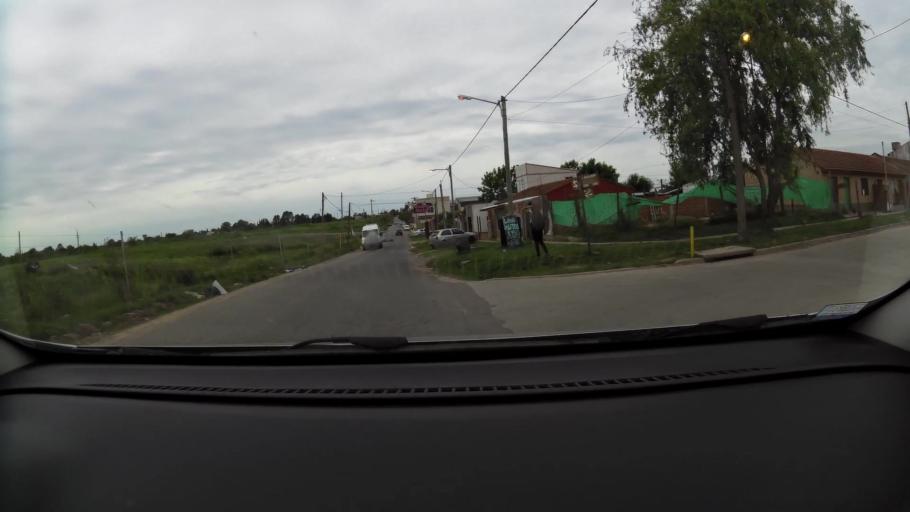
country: AR
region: Buenos Aires
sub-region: Partido de Campana
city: Campana
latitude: -34.2038
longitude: -58.9467
